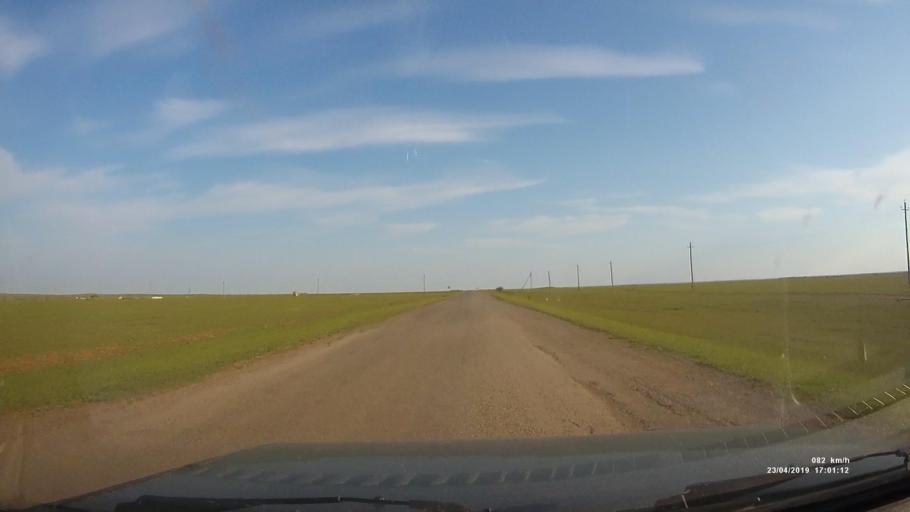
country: RU
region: Kalmykiya
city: Priyutnoye
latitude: 46.2988
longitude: 43.4073
